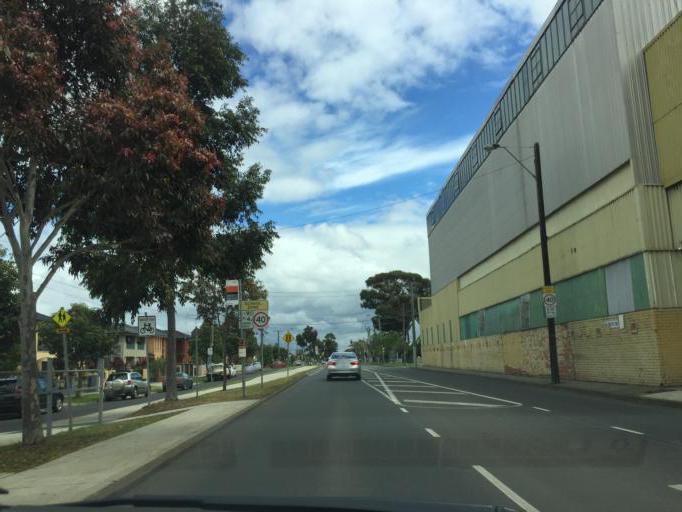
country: AU
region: Victoria
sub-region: Maribyrnong
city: Braybrook
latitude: -37.7922
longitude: 144.8585
